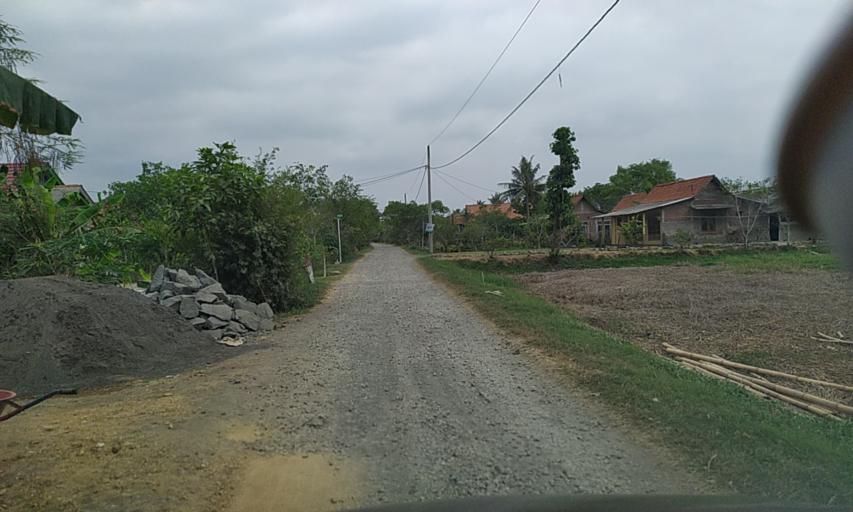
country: ID
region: Central Java
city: Sidakaya
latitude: -7.6429
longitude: 108.9005
